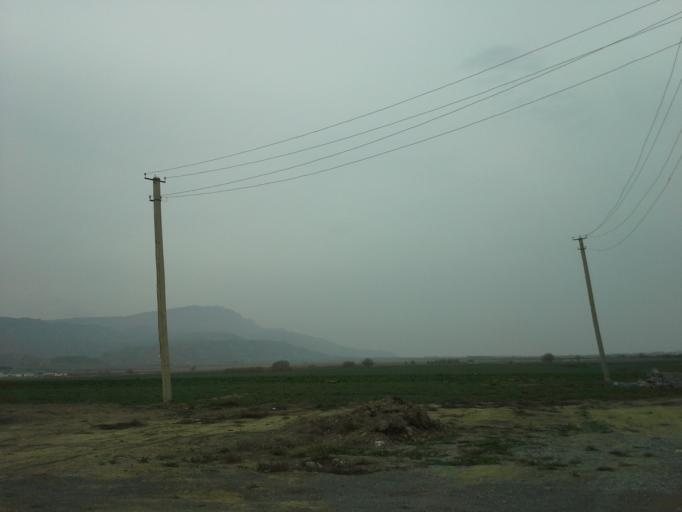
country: TM
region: Ahal
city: Abadan
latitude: 37.9822
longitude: 58.2177
